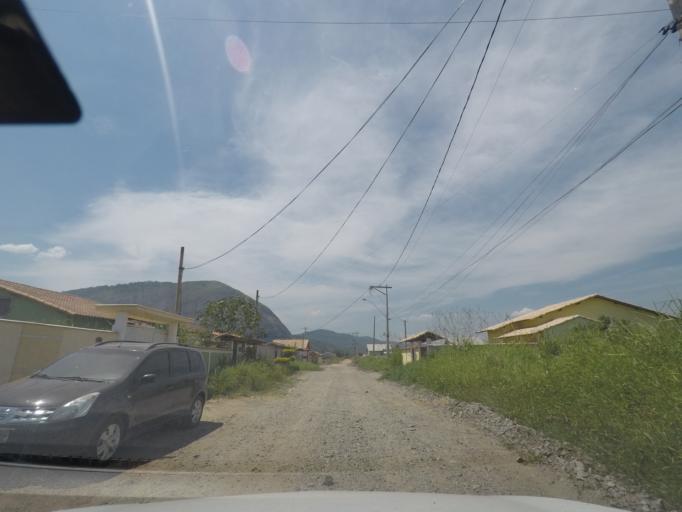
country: BR
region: Rio de Janeiro
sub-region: Marica
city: Marica
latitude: -22.9527
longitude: -42.9550
